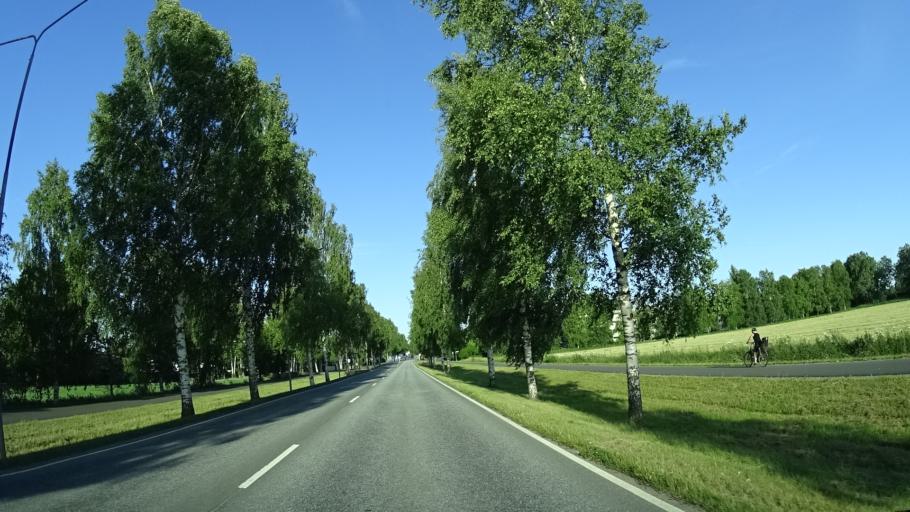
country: FI
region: Satakunta
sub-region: Pori
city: Kokemaeki
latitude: 61.2578
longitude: 22.3325
